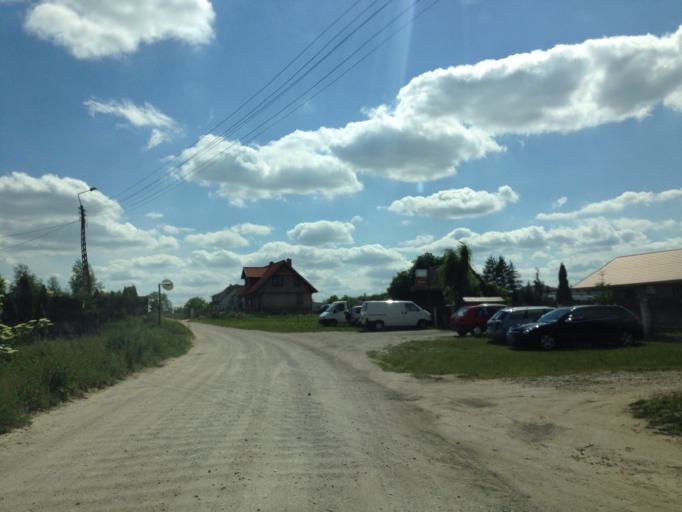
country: PL
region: Kujawsko-Pomorskie
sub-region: Powiat brodnicki
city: Gorzno
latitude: 53.1936
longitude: 19.6382
